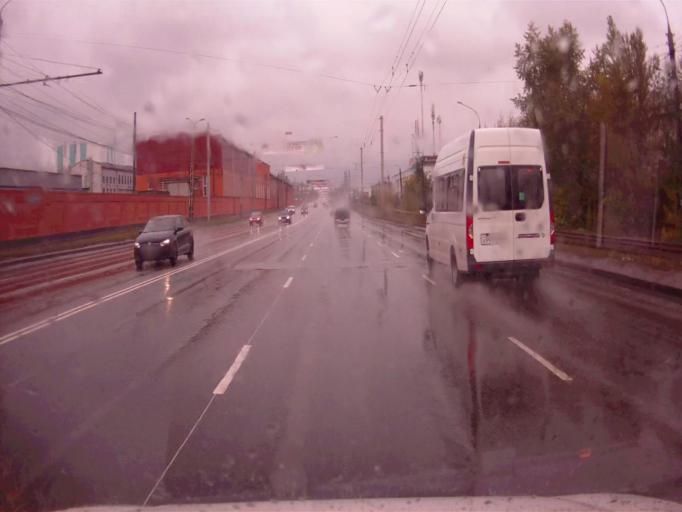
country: RU
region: Chelyabinsk
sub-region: Gorod Chelyabinsk
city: Chelyabinsk
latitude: 55.2063
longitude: 61.3847
